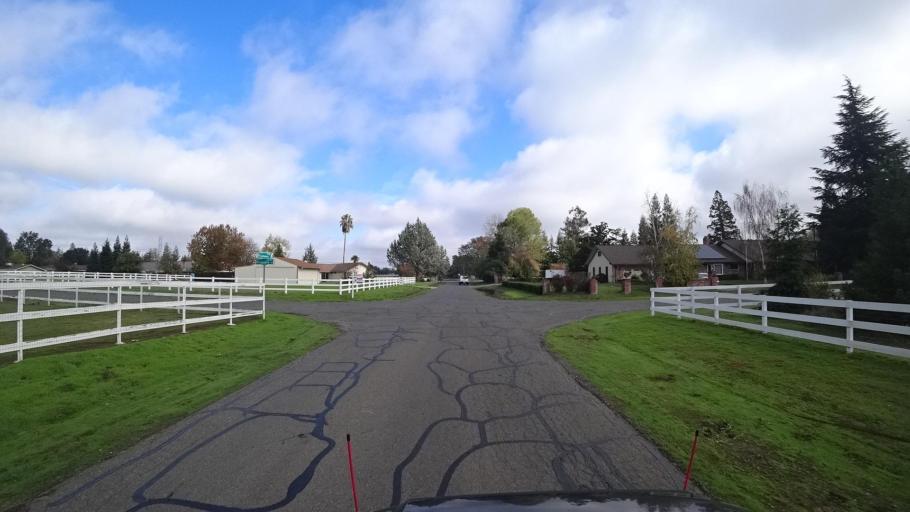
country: US
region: California
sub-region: Sacramento County
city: Vineyard
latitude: 38.4345
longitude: -121.3266
